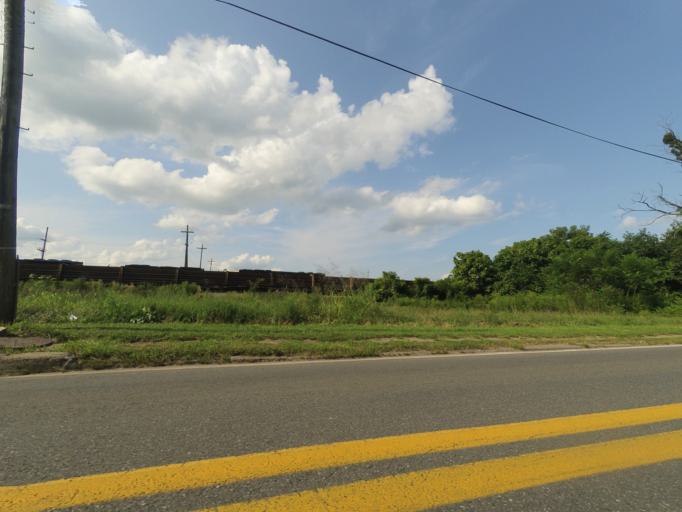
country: US
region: West Virginia
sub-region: Cabell County
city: Huntington
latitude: 38.4215
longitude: -82.4067
